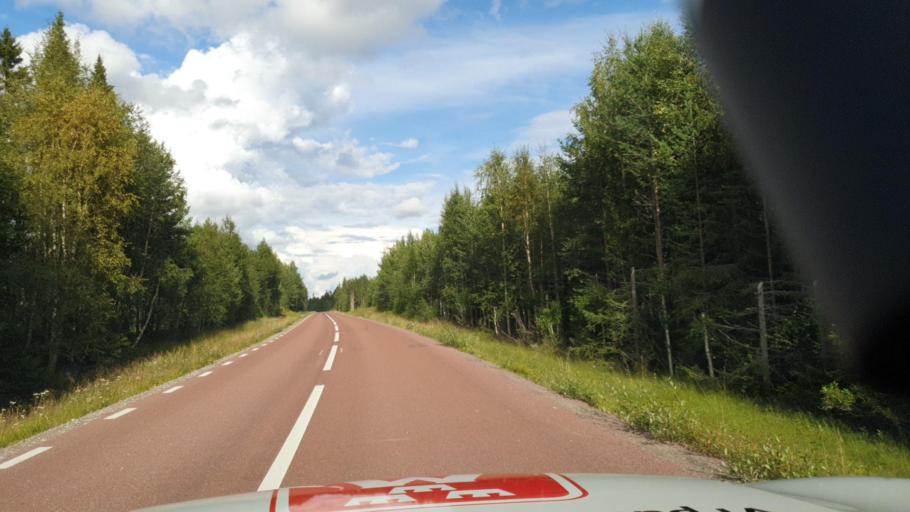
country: SE
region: Jaemtland
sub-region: Harjedalens Kommun
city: Sveg
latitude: 62.1118
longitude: 13.7550
